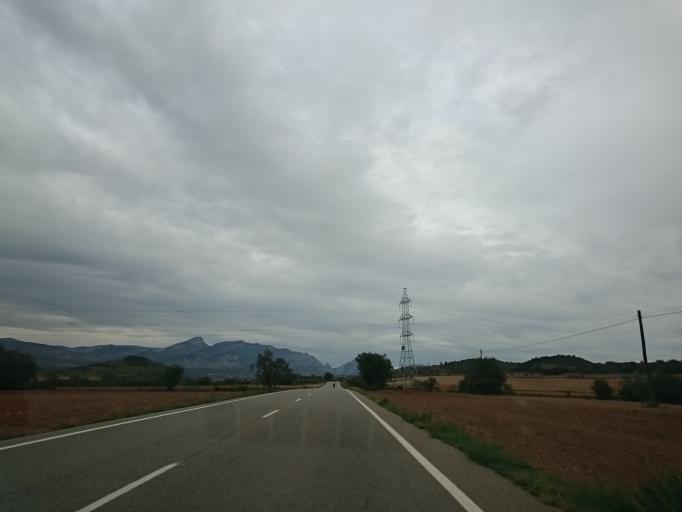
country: ES
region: Catalonia
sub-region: Provincia de Lleida
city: Llimiana
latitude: 42.1298
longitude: 0.9650
